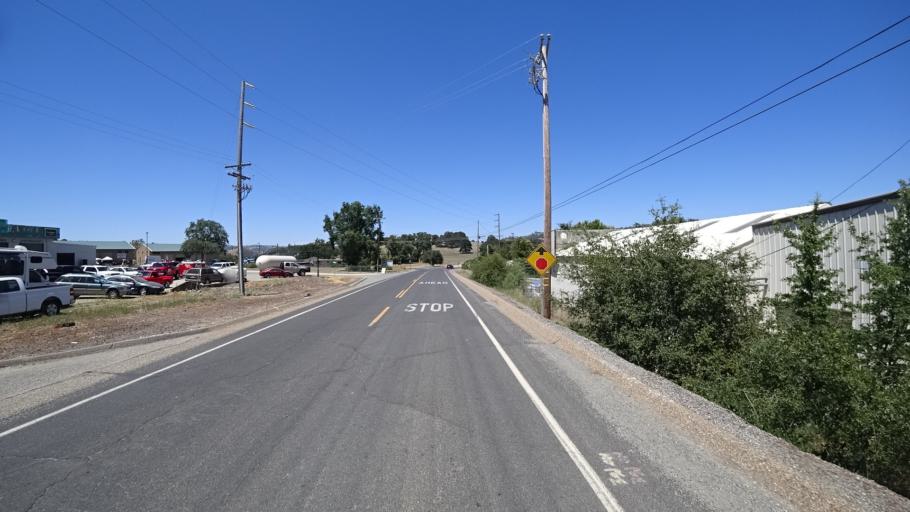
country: US
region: California
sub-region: Calaveras County
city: San Andreas
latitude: 38.1998
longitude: -120.6926
